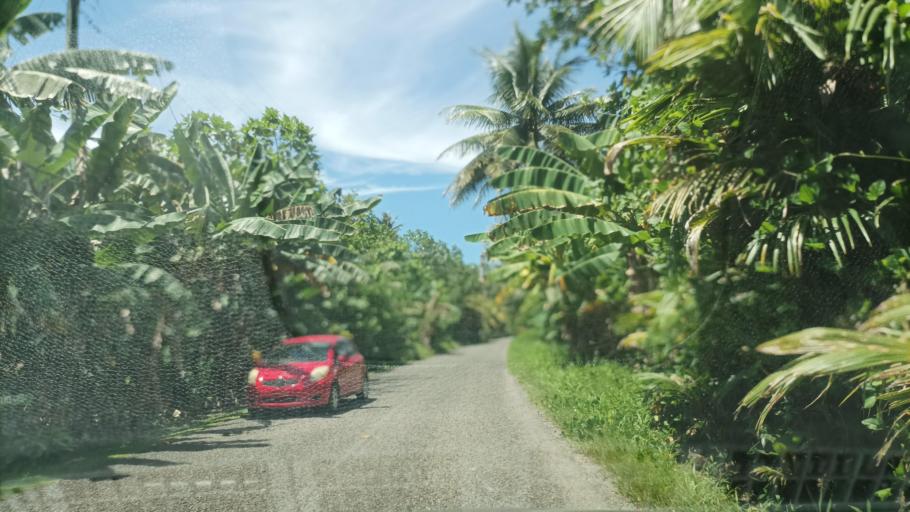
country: FM
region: Kosrae
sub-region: Malem Municipality
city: Malem
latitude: 5.3000
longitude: 163.0300
